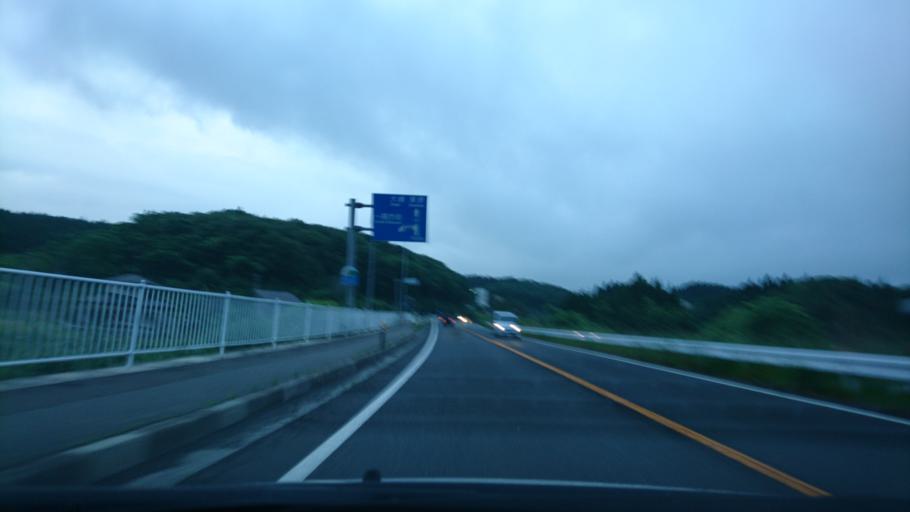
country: JP
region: Iwate
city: Ichinoseki
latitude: 38.8899
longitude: 141.1168
